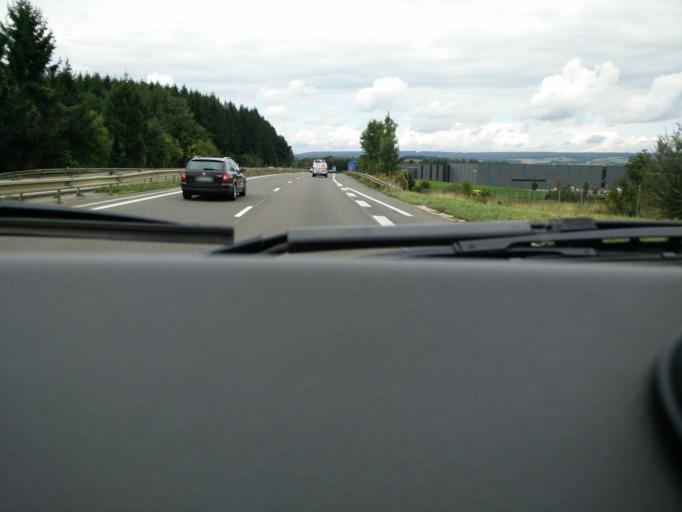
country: FR
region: Champagne-Ardenne
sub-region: Departement des Ardennes
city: Donchery
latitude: 49.6986
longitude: 4.9043
